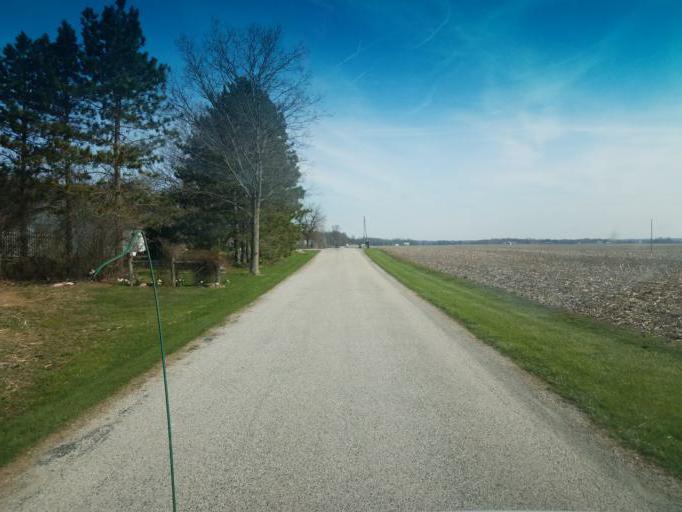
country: US
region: Ohio
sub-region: Richland County
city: Shelby
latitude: 40.8856
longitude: -82.5714
